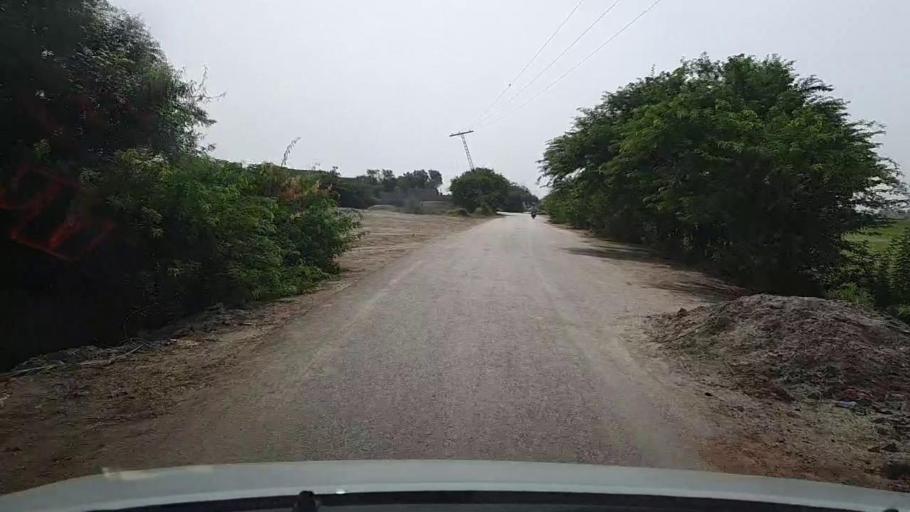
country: PK
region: Sindh
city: Mehar
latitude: 27.1211
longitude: 67.8486
